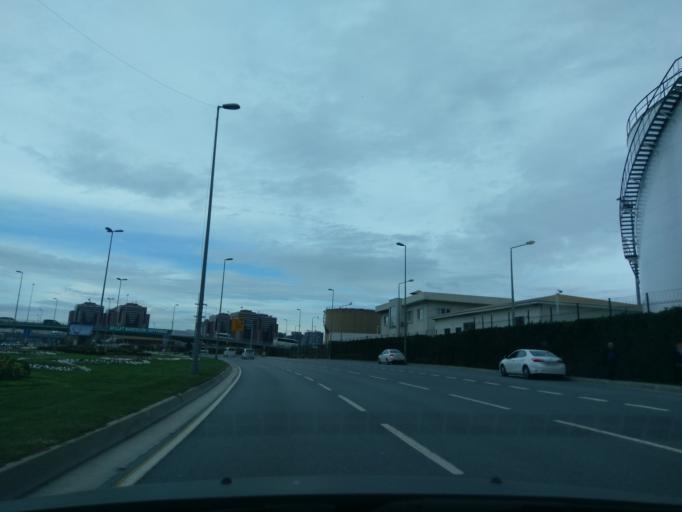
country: TR
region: Istanbul
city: Bahcelievler
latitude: 40.9816
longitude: 28.8399
